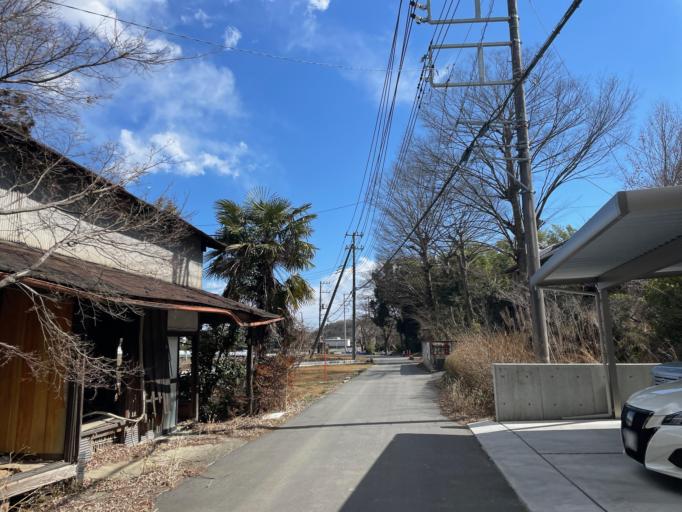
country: JP
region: Saitama
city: Sakado
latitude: 36.0189
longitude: 139.3779
